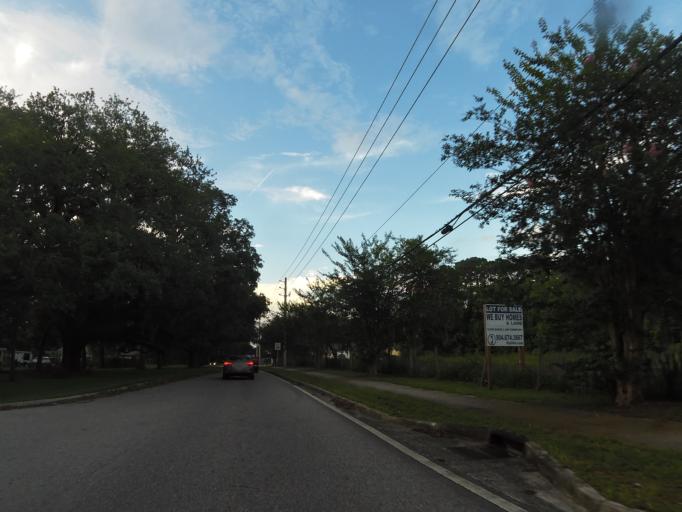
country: US
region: Florida
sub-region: Duval County
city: Jacksonville
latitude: 30.2653
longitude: -81.5921
